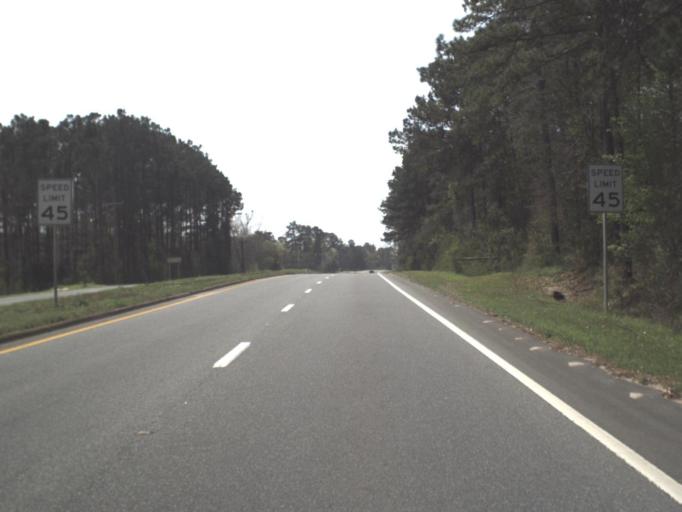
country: US
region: Florida
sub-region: Gadsden County
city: Havana
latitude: 30.6459
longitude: -84.4170
